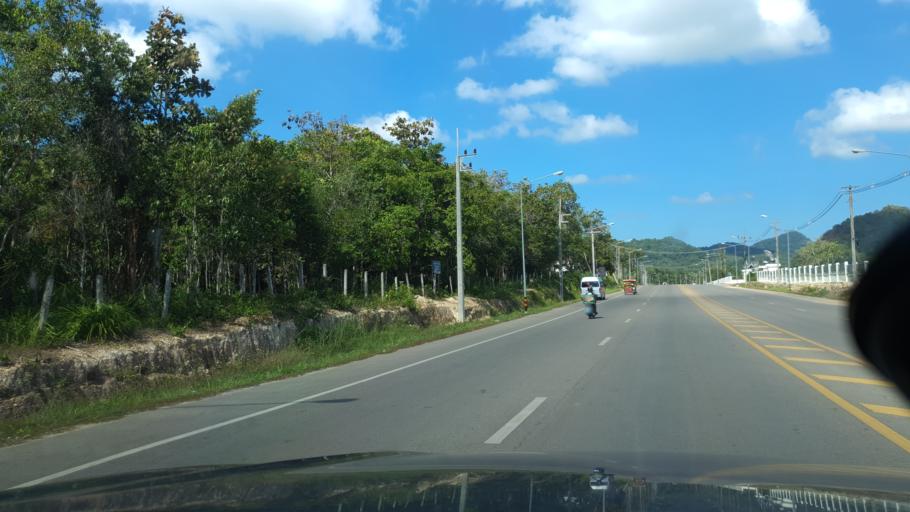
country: TH
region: Phangnga
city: Ban Ao Nang
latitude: 8.0391
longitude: 98.8518
